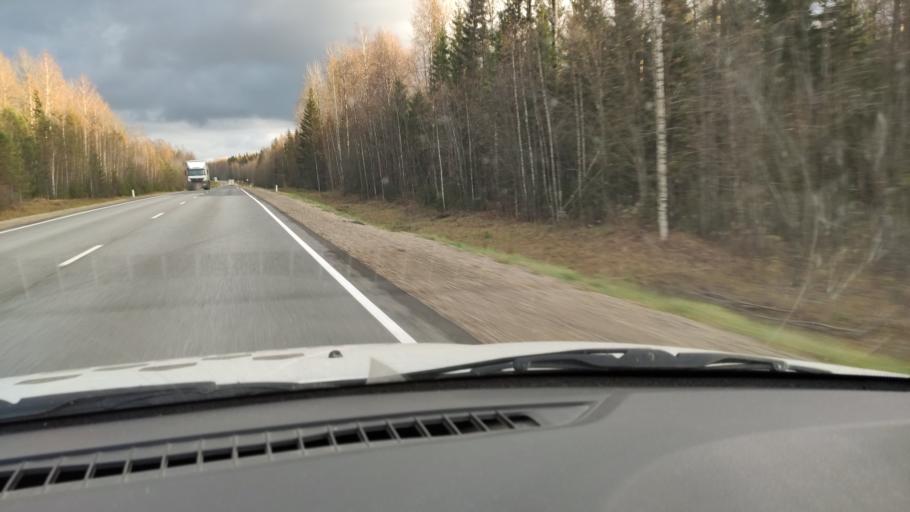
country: RU
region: Kirov
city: Chernaya Kholunitsa
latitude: 58.7804
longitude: 51.9147
